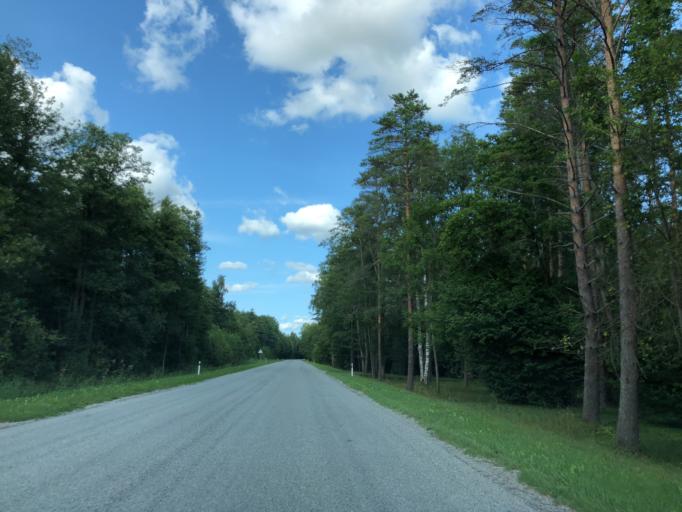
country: EE
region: Hiiumaa
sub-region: Kaerdla linn
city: Kardla
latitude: 58.8167
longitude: 22.7375
